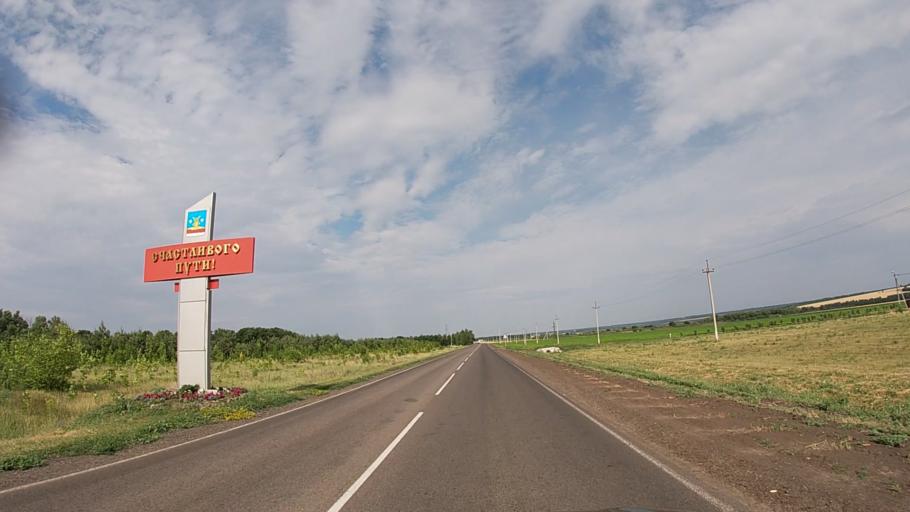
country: RU
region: Belgorod
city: Krasnaya Yaruga
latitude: 50.7976
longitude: 35.6294
